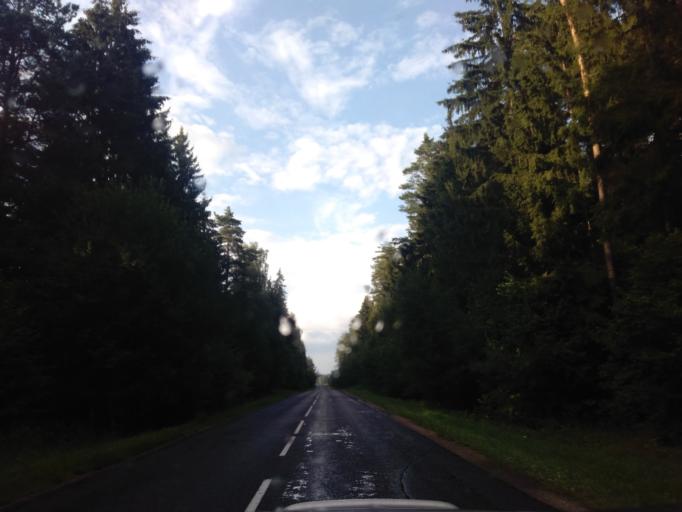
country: BY
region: Minsk
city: Kapyl'
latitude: 53.2733
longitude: 27.0760
